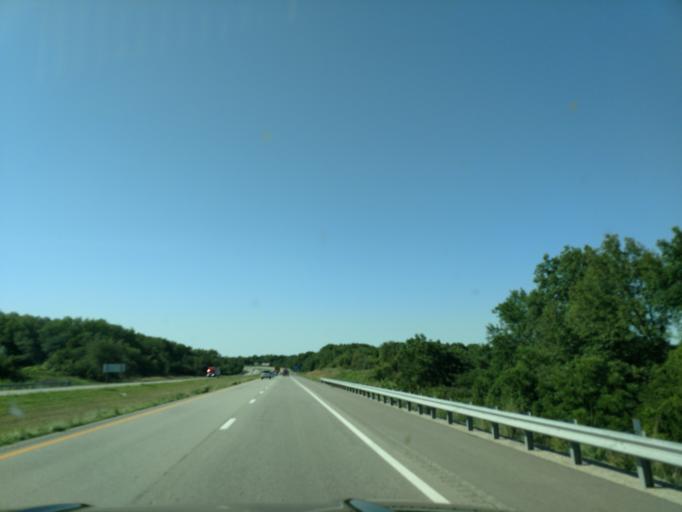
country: US
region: Missouri
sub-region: Andrew County
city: Country Club Village
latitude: 39.8462
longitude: -94.8051
